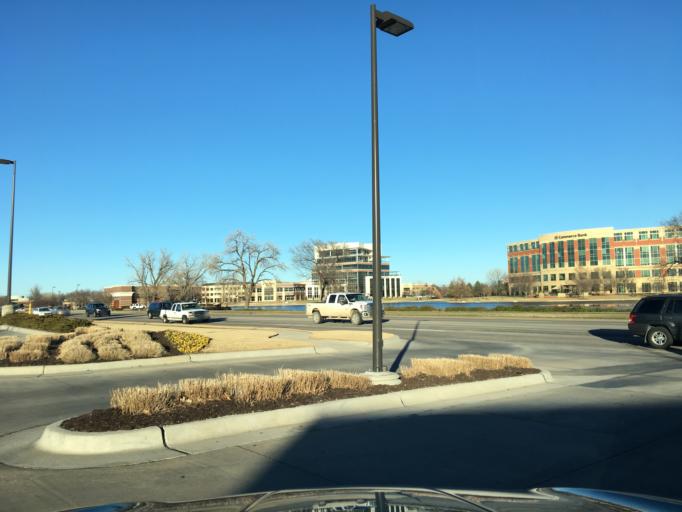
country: US
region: Kansas
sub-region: Sedgwick County
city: Bellaire
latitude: 37.7098
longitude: -97.2266
